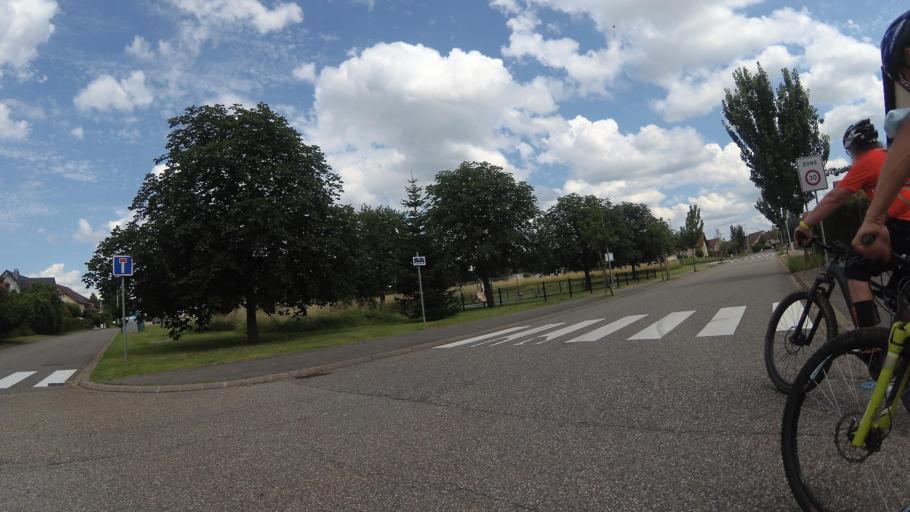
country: FR
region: Lorraine
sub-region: Departement de la Moselle
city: Sarreguemines
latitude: 49.1201
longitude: 7.0975
